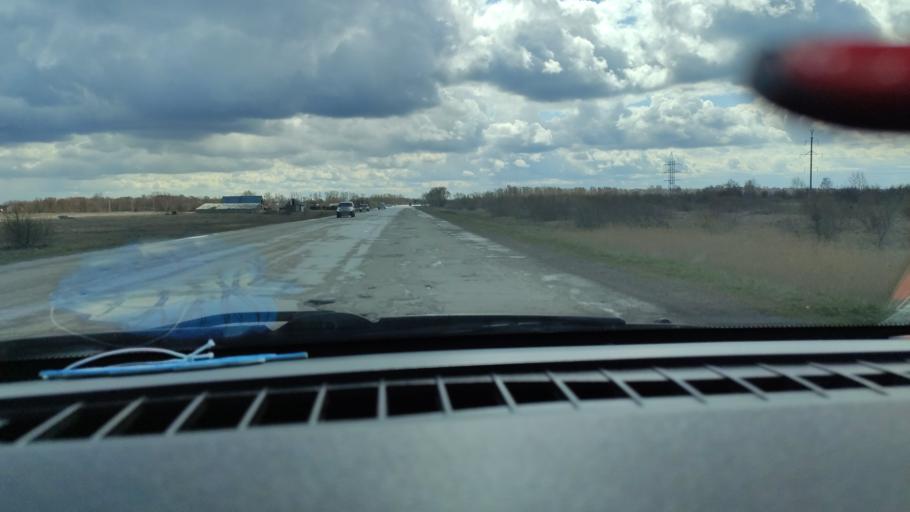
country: RU
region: Samara
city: Tol'yatti
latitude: 53.6635
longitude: 49.4225
